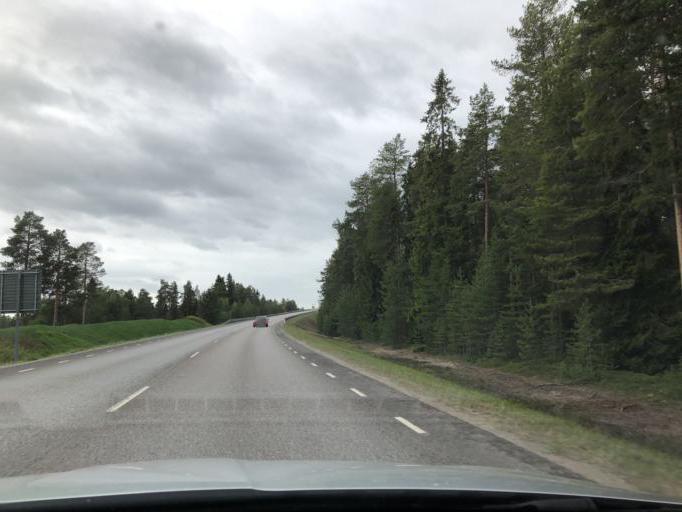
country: SE
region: Norrbotten
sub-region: Pitea Kommun
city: Pitea
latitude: 65.2350
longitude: 21.5236
